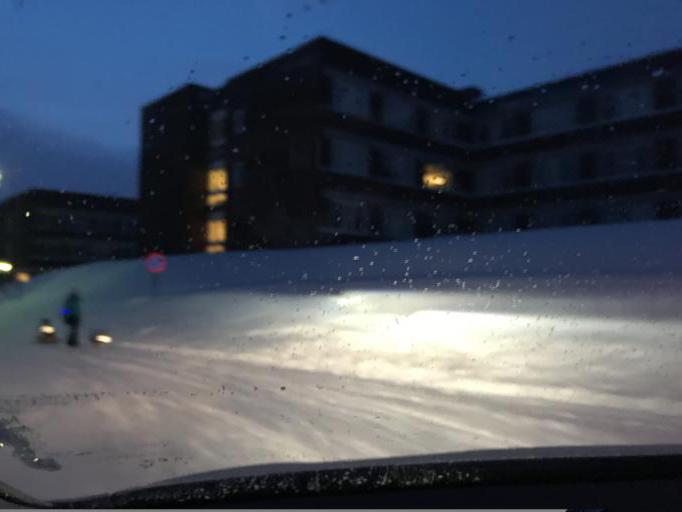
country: SE
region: Norrbotten
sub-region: Kiruna Kommun
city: Kiruna
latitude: 67.8484
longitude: 20.2324
